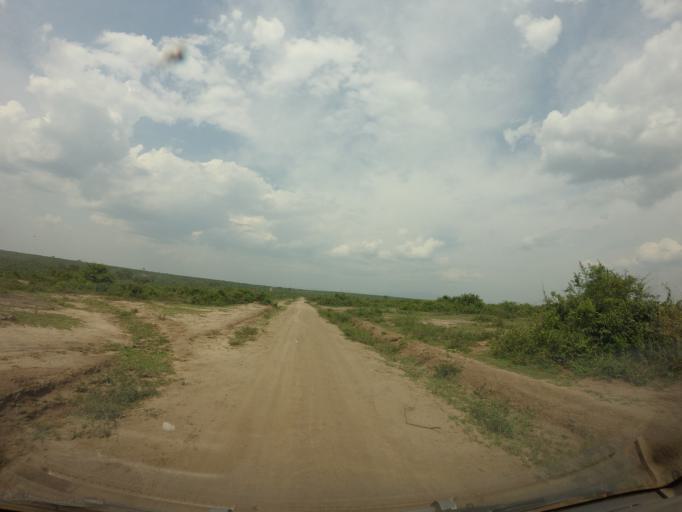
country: UG
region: Western Region
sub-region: Rubirizi District
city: Rubirizi
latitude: -0.2098
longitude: 29.9057
